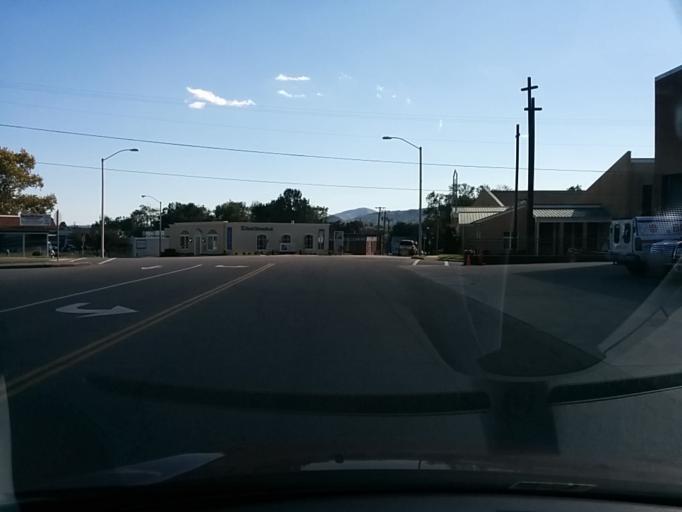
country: US
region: Virginia
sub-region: City of Salem
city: Salem
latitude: 37.2920
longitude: -80.0564
